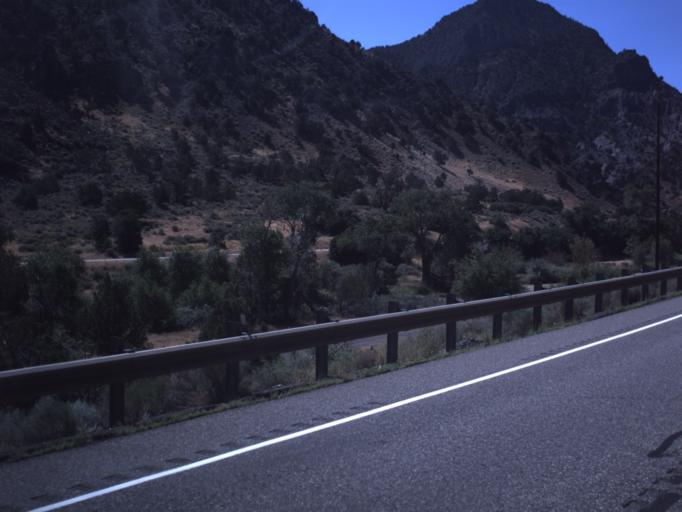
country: US
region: Utah
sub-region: Sevier County
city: Monroe
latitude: 38.5460
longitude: -112.2691
